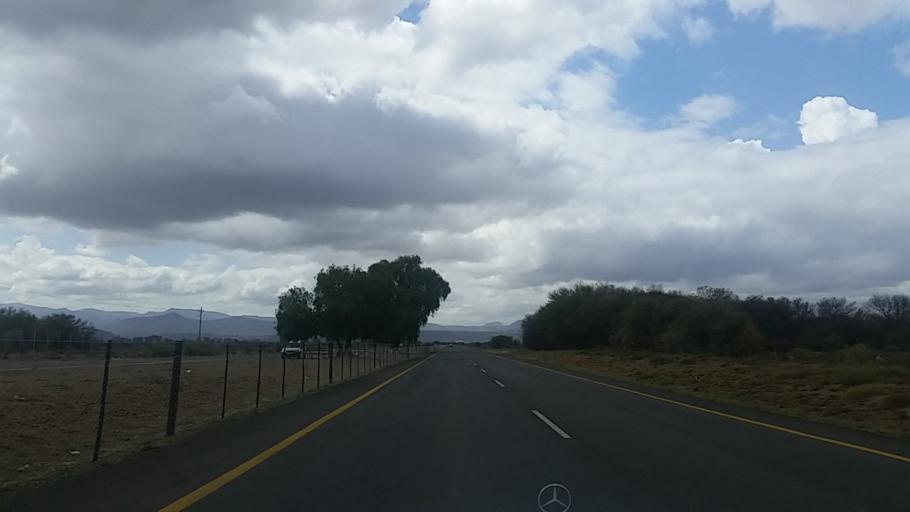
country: ZA
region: Eastern Cape
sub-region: Cacadu District Municipality
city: Graaff-Reinet
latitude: -32.2104
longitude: 24.5475
